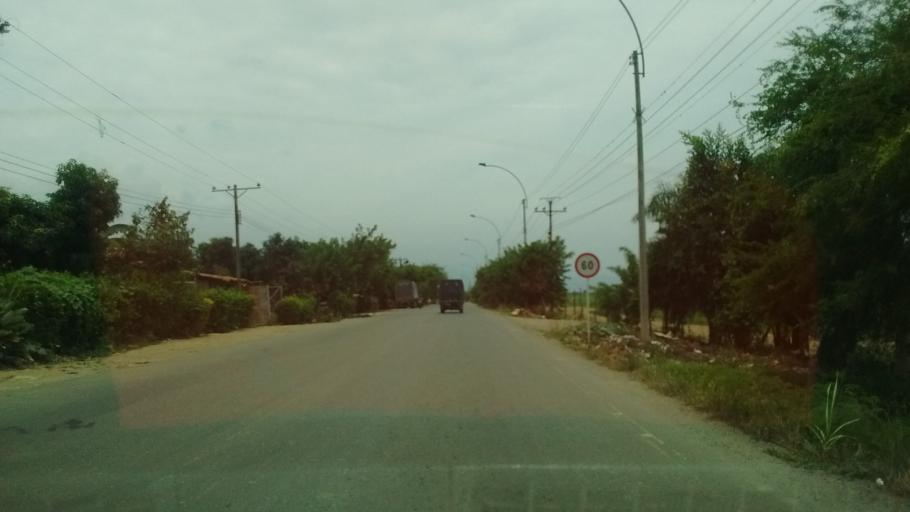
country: CO
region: Valle del Cauca
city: Jamundi
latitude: 3.3036
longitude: -76.4788
